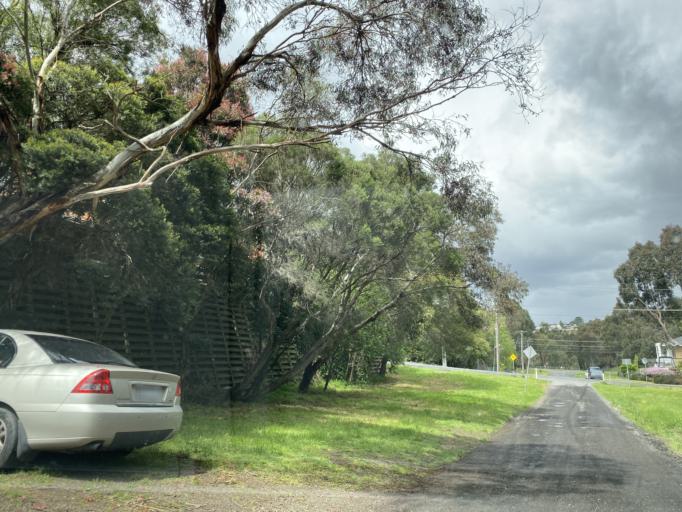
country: AU
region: Victoria
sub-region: Banyule
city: Darch
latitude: -37.7569
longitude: 145.1252
